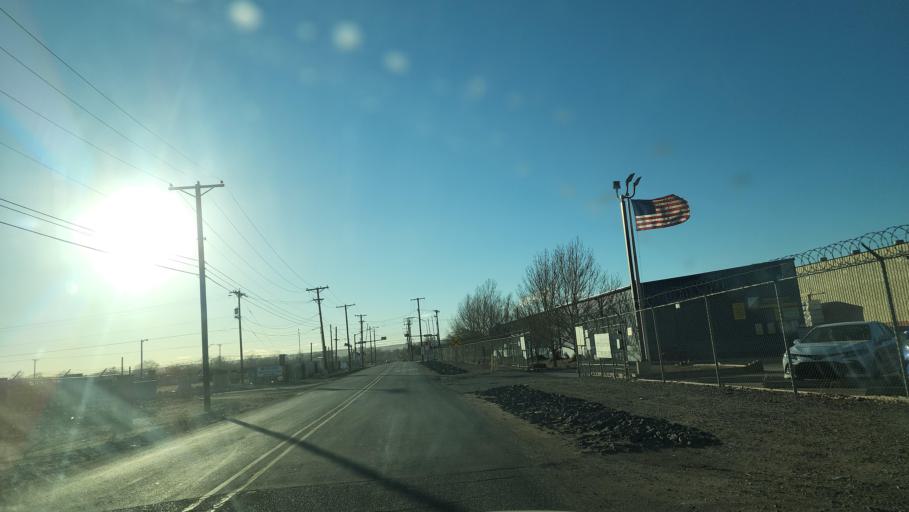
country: US
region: New Mexico
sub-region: Bernalillo County
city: South Valley
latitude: 35.0151
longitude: -106.6587
